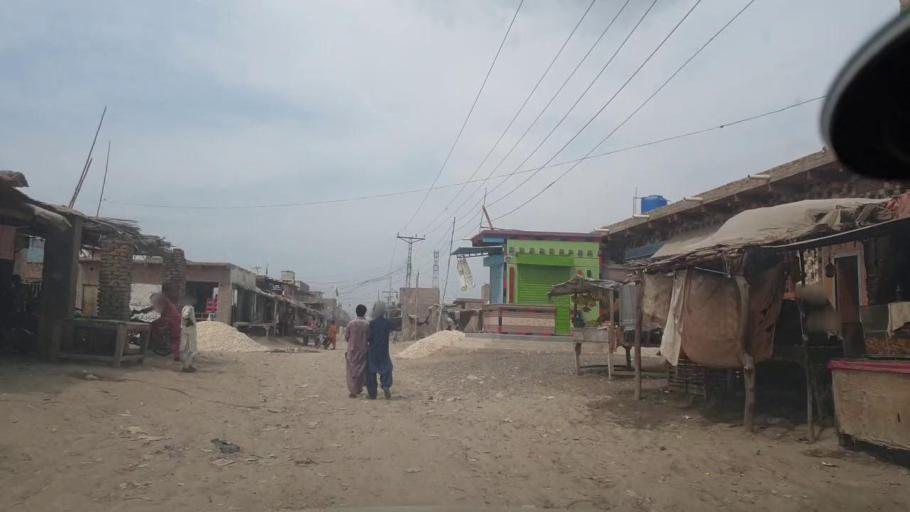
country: PK
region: Sindh
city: Jacobabad
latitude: 28.2666
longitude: 68.4377
